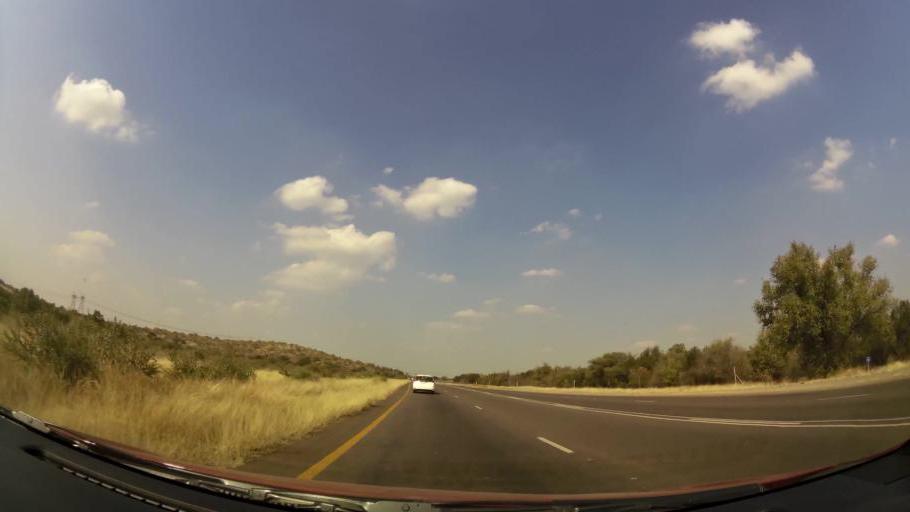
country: ZA
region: North-West
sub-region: Bojanala Platinum District Municipality
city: Mogwase
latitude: -25.4337
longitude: 27.0845
